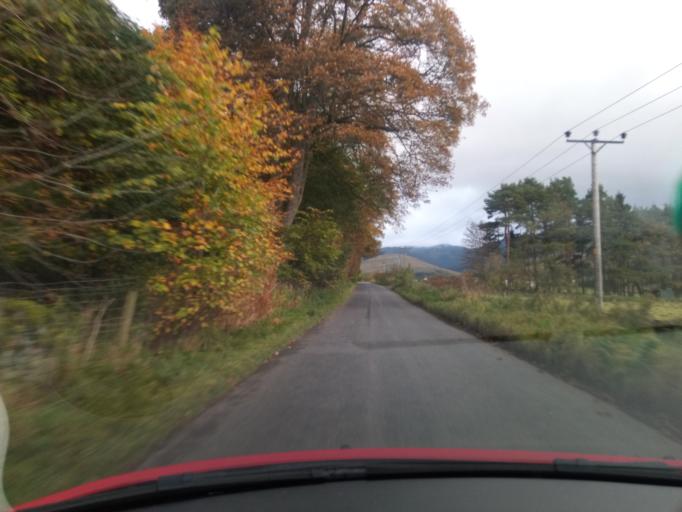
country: GB
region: Scotland
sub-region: The Scottish Borders
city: Innerleithen
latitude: 55.6306
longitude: -3.1042
